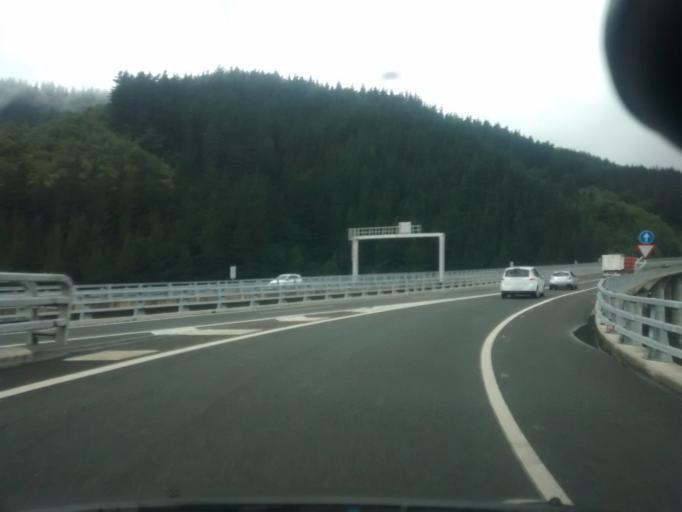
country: ES
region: Basque Country
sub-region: Provincia de Guipuzcoa
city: Bergara
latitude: 43.0911
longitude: -2.4344
